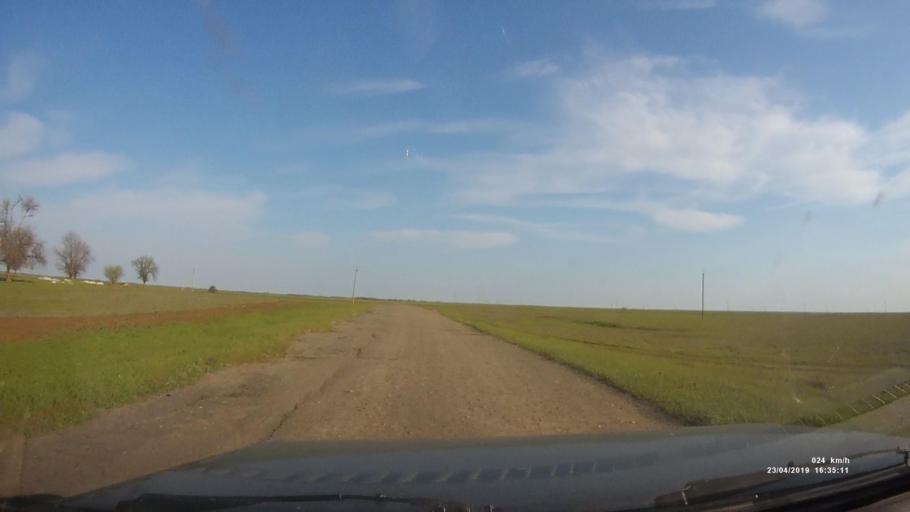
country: RU
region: Kalmykiya
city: Priyutnoye
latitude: 46.3318
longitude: 43.1365
